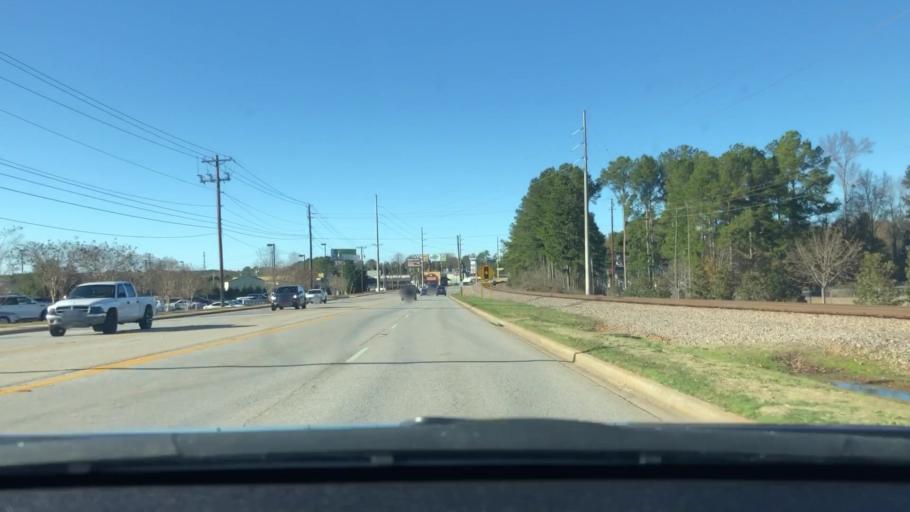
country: US
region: South Carolina
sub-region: Lexington County
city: Irmo
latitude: 34.0696
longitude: -81.1731
